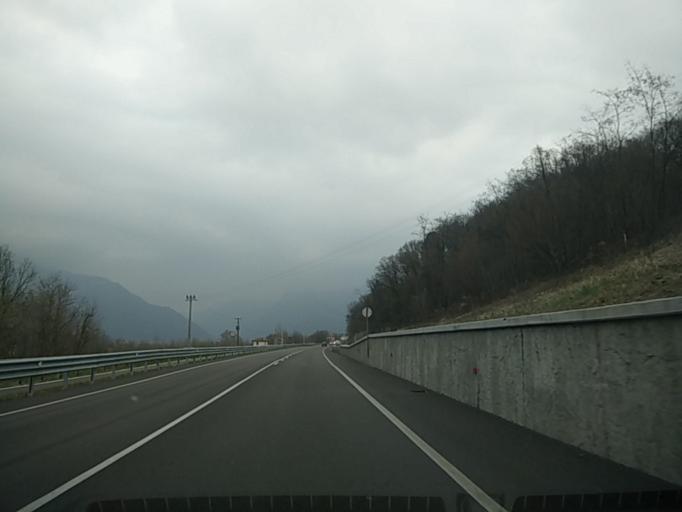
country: IT
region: Veneto
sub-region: Provincia di Belluno
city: Castion
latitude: 46.1377
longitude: 12.2321
